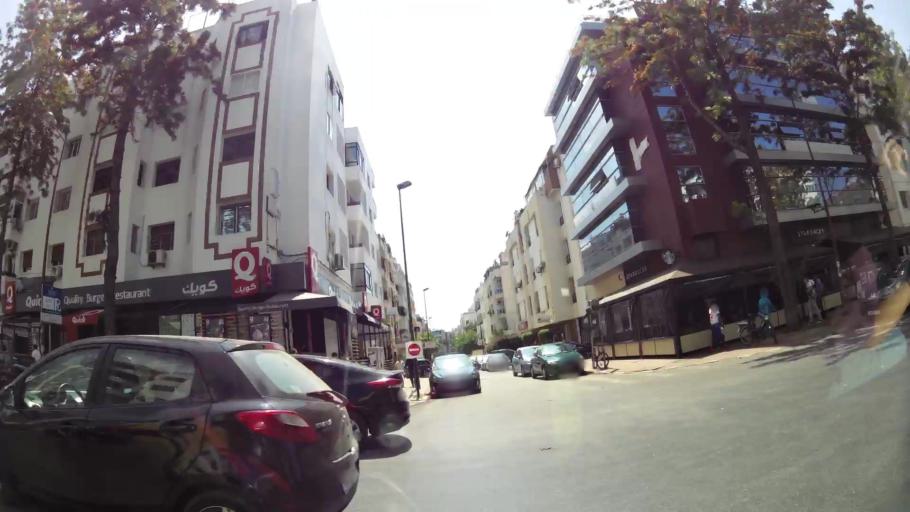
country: MA
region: Rabat-Sale-Zemmour-Zaer
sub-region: Rabat
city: Rabat
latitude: 33.9957
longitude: -6.8478
